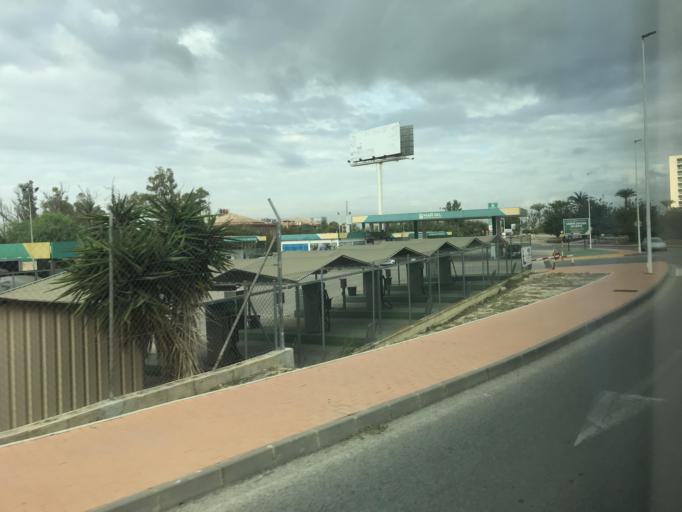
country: ES
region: Valencia
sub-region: Provincia de Alicante
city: Guardamar del Segura
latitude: 38.0937
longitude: -0.6600
